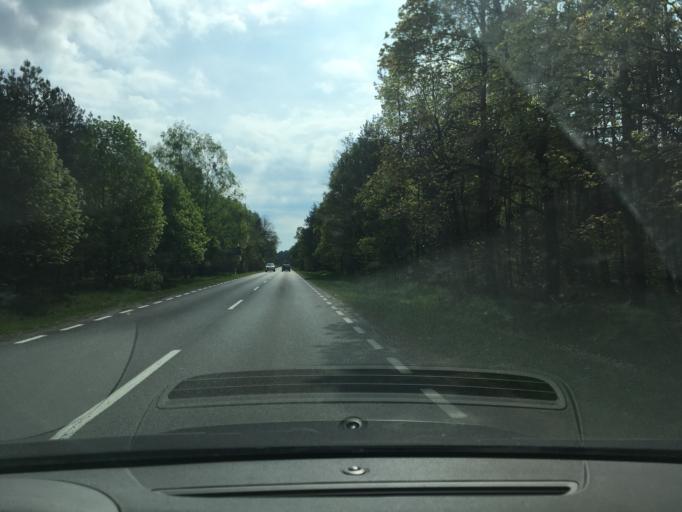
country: PL
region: Lublin Voivodeship
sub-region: Powiat rycki
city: Stezyca
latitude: 51.5925
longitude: 21.7415
